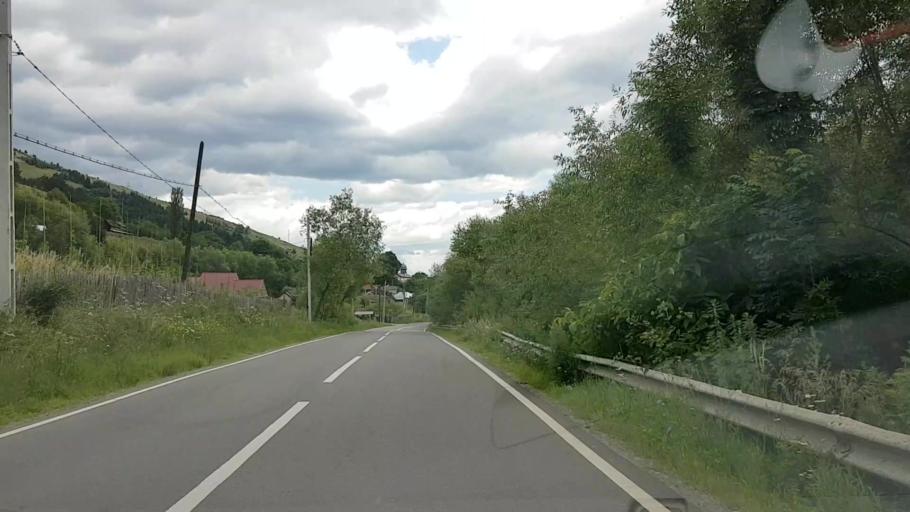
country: RO
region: Neamt
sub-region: Comuna Farcasa
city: Farcasa
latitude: 47.1696
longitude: 25.8004
